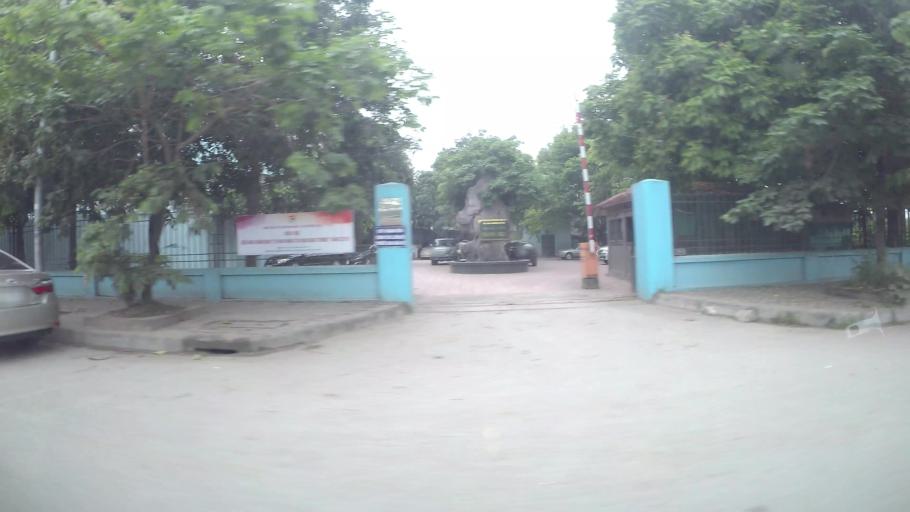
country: VN
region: Ha Noi
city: Hai BaTrung
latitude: 20.9815
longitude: 105.8903
